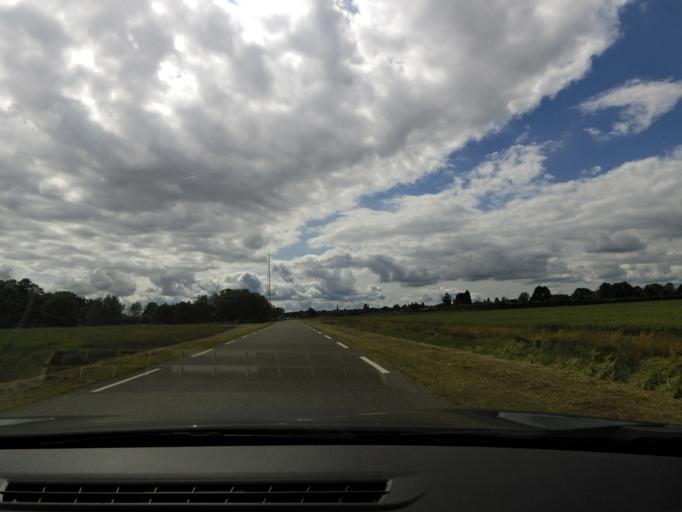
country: NL
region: South Holland
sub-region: Gemeente Strijen
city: Strijen
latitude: 51.7467
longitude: 4.5647
